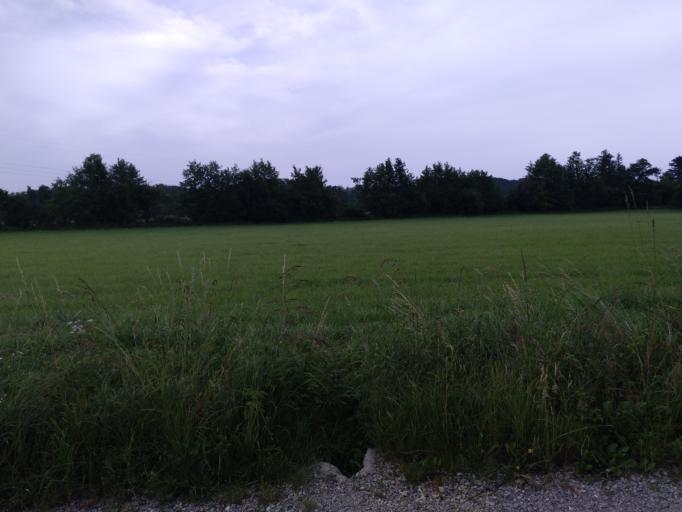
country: FR
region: Rhone-Alpes
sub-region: Departement du Rhone
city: Marennes
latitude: 45.6343
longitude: 4.9249
